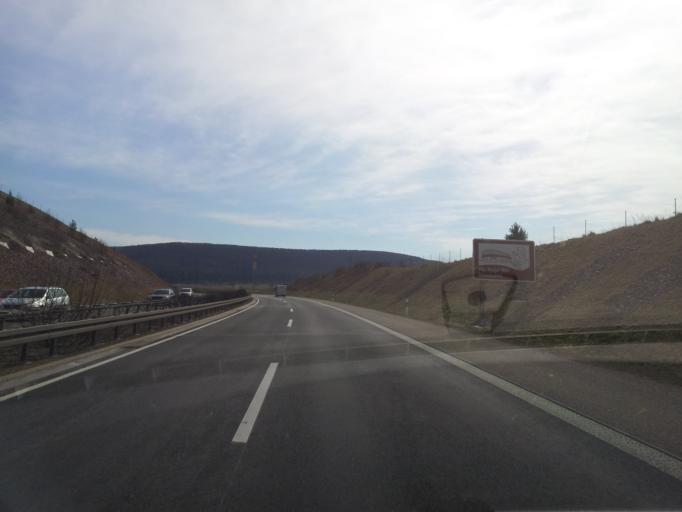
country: DE
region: Thuringia
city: Ellingshausen
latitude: 50.5377
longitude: 10.4757
